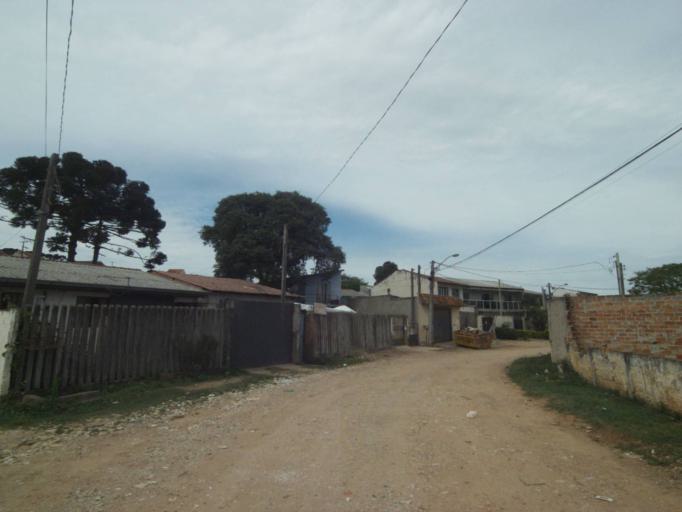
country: BR
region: Parana
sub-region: Pinhais
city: Pinhais
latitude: -25.4281
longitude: -49.2075
